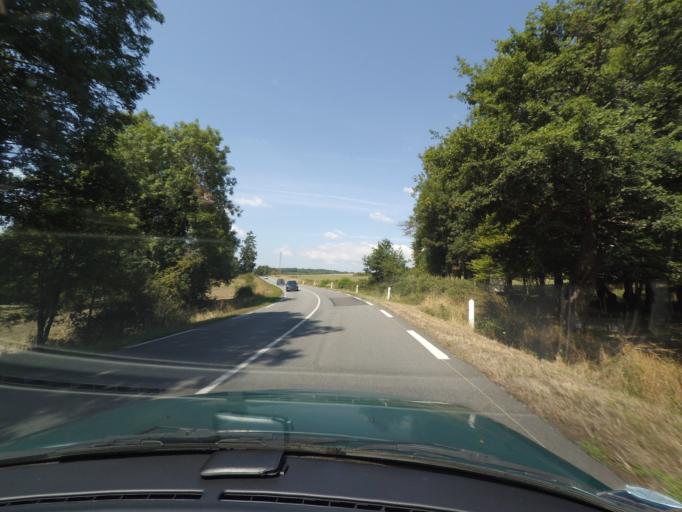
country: FR
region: Limousin
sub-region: Departement de la Haute-Vienne
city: Feytiat
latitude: 45.8054
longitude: 1.3688
